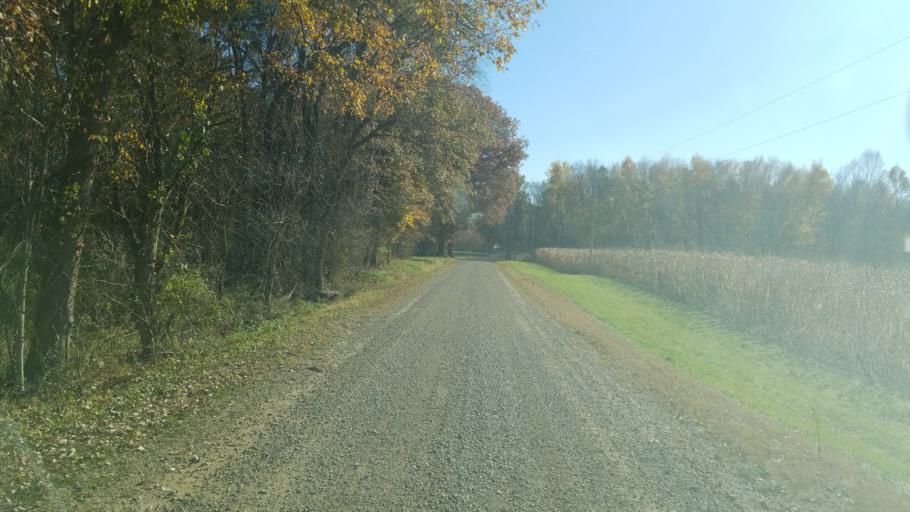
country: US
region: Ohio
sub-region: Knox County
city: Danville
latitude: 40.4427
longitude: -82.2916
